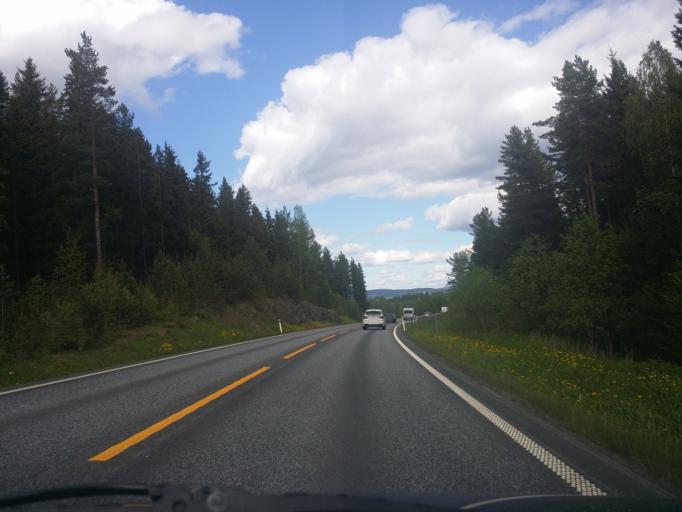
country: NO
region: Oppland
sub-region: Lunner
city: Roa
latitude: 60.2772
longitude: 10.5133
